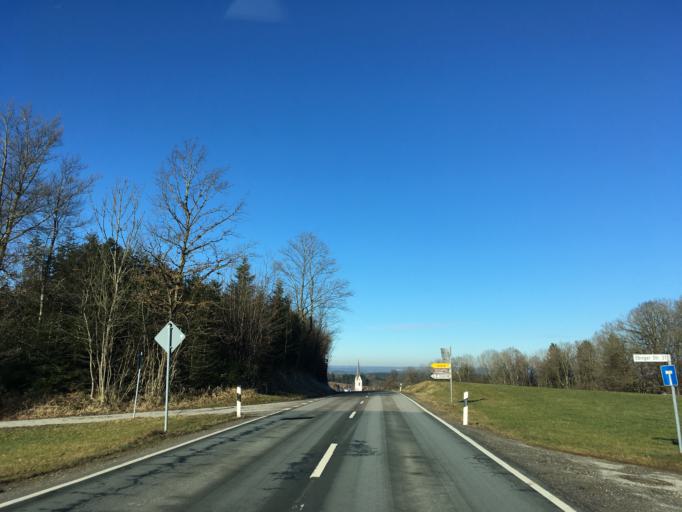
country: DE
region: Bavaria
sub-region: Upper Bavaria
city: Amerang
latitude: 47.9884
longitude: 12.3153
